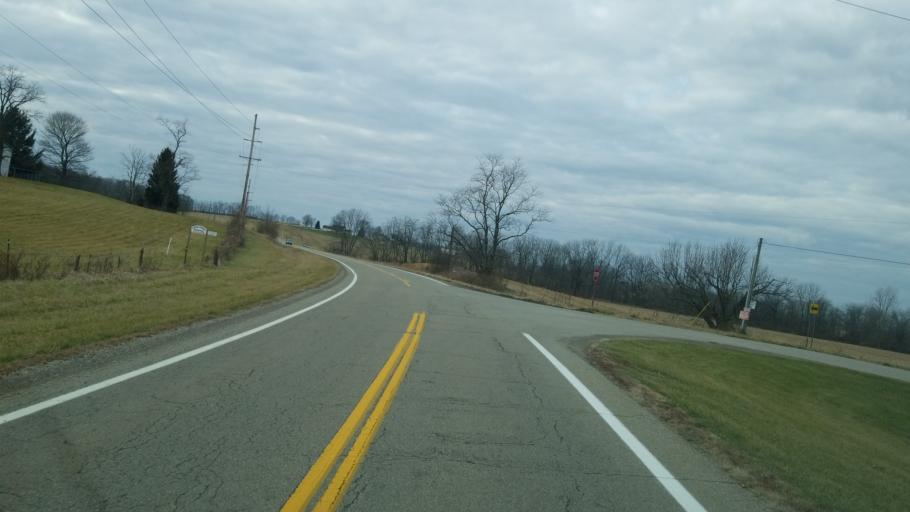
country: US
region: Ohio
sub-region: Ross County
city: Frankfort
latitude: 39.3563
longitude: -83.2751
